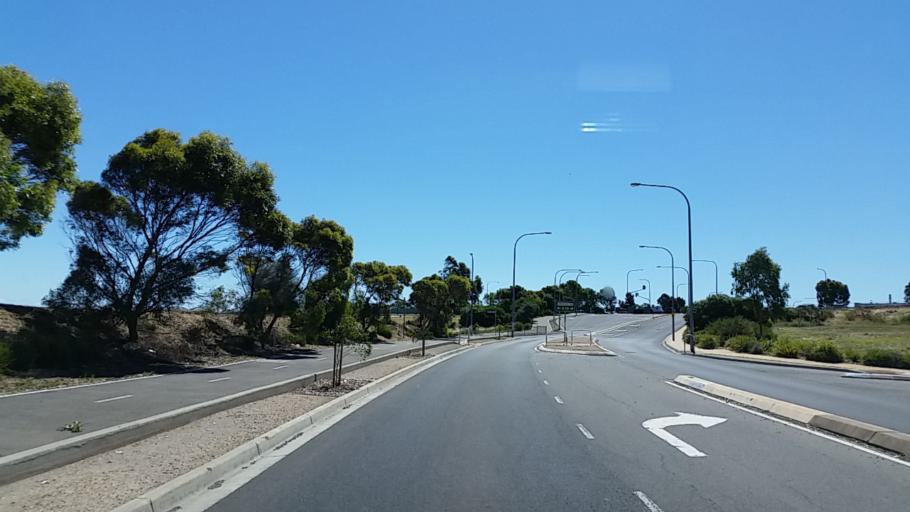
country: AU
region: South Australia
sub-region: Marion
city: Happy Valley
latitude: -35.0798
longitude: 138.5189
